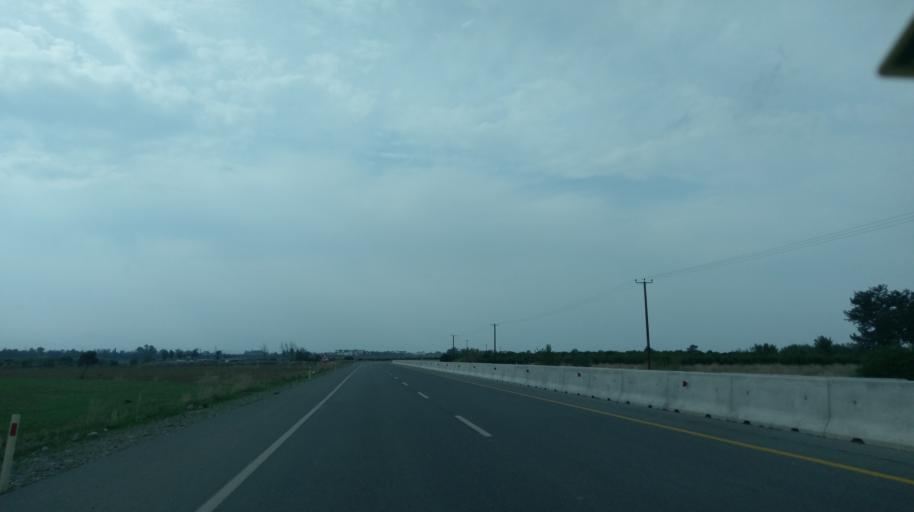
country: CY
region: Lefkosia
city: Morfou
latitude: 35.1994
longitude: 33.0248
